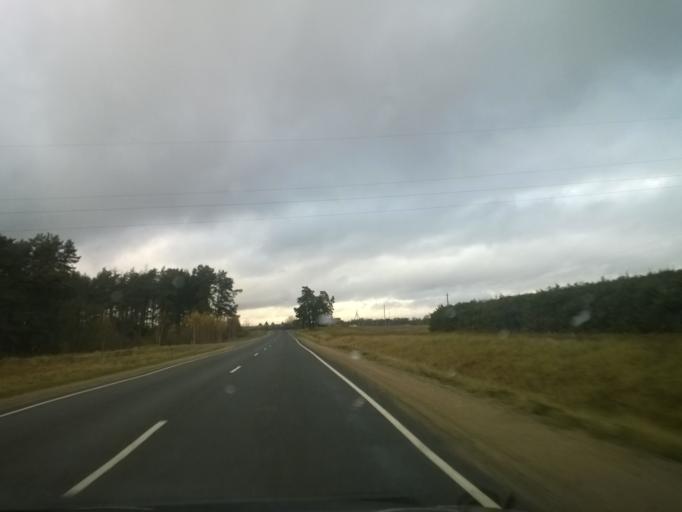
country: BY
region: Grodnenskaya
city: Mir
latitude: 53.4384
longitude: 26.4794
